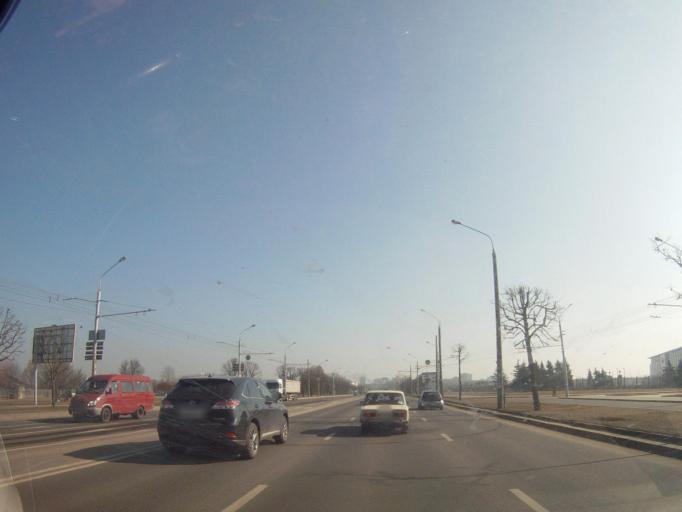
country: BY
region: Minsk
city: Minsk
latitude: 53.9295
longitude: 27.5213
